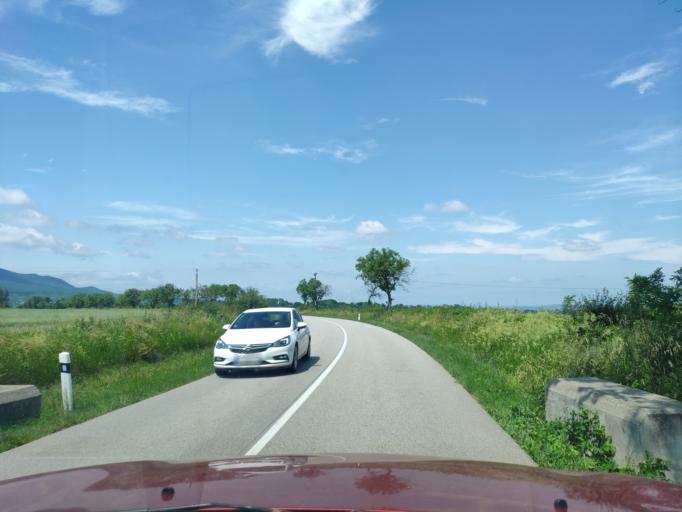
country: SK
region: Kosicky
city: Secovce
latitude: 48.7366
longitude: 21.6503
